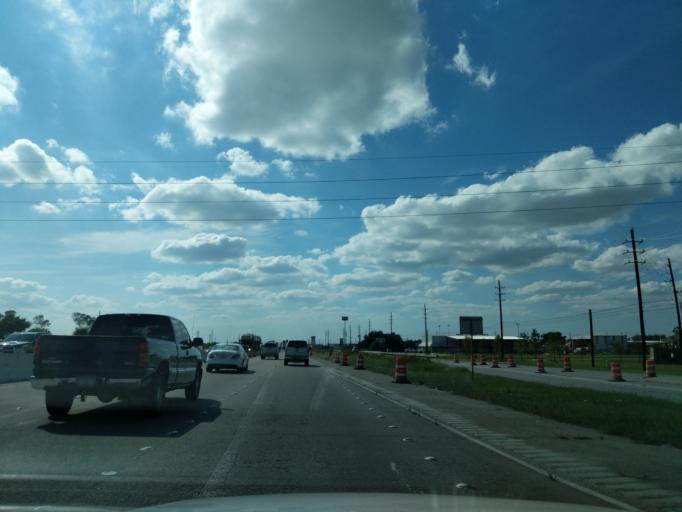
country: US
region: Texas
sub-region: Chambers County
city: Old River-Winfree
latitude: 29.8270
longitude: -94.8406
